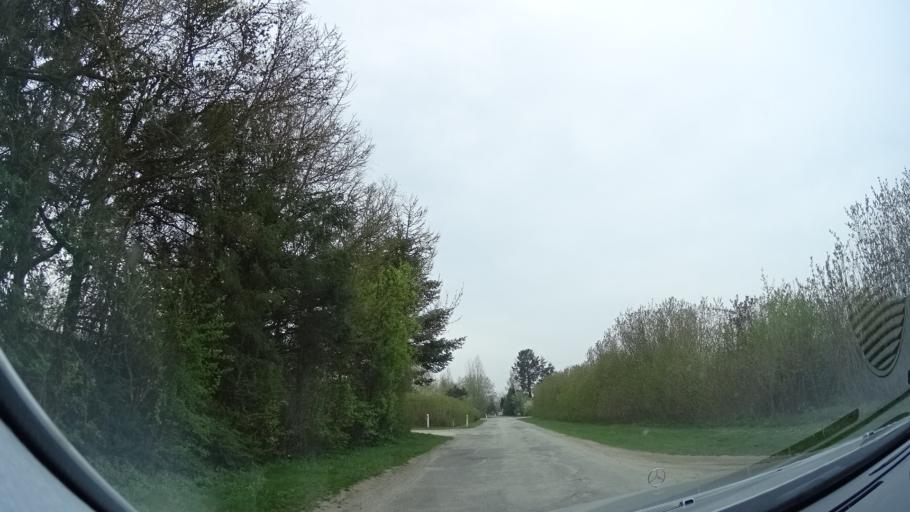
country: DK
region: Zealand
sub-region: Lejre Kommune
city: Ejby
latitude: 55.7095
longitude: 11.8481
